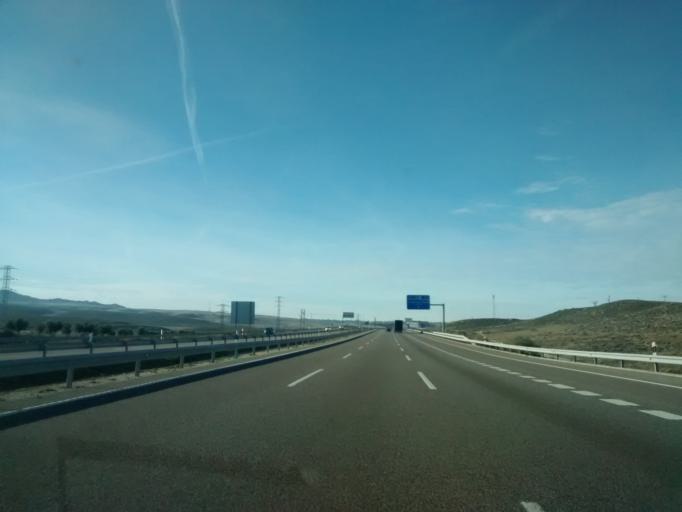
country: ES
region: Aragon
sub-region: Provincia de Zaragoza
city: Maria de Huerva
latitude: 41.6205
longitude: -1.0284
